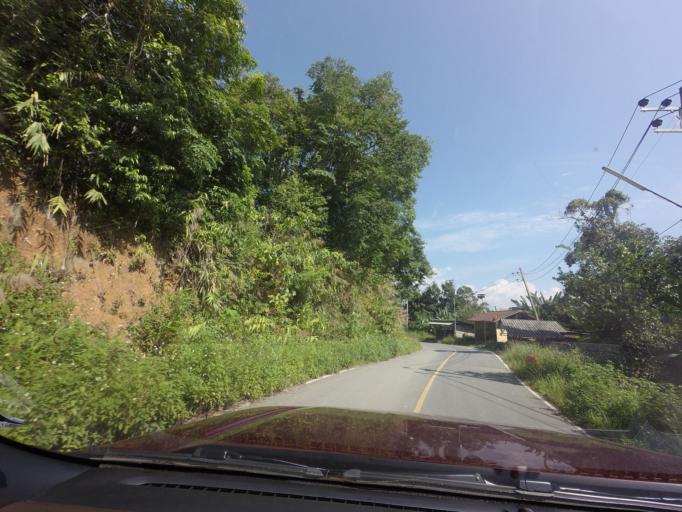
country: TH
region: Yala
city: Than To
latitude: 5.9977
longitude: 101.2167
